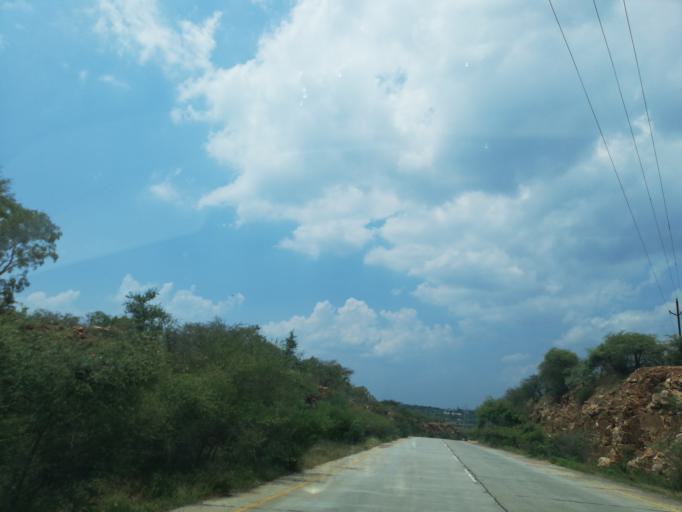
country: IN
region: Andhra Pradesh
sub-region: Guntur
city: Macherla
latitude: 16.5708
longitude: 79.3319
